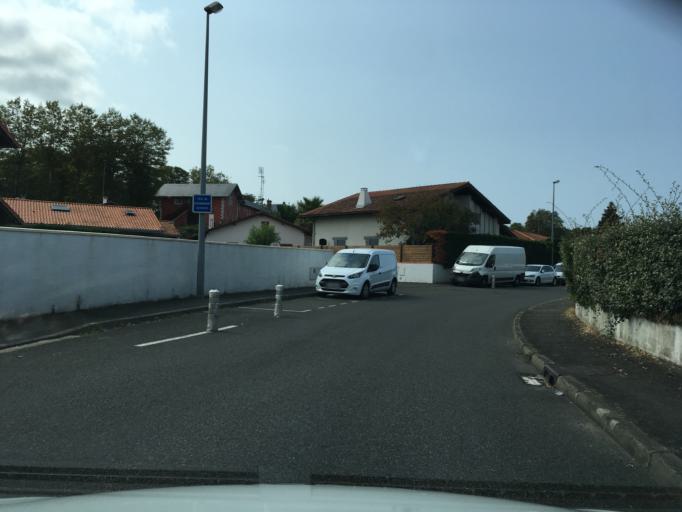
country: FR
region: Aquitaine
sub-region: Departement des Pyrenees-Atlantiques
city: Anglet
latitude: 43.4845
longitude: -1.5183
